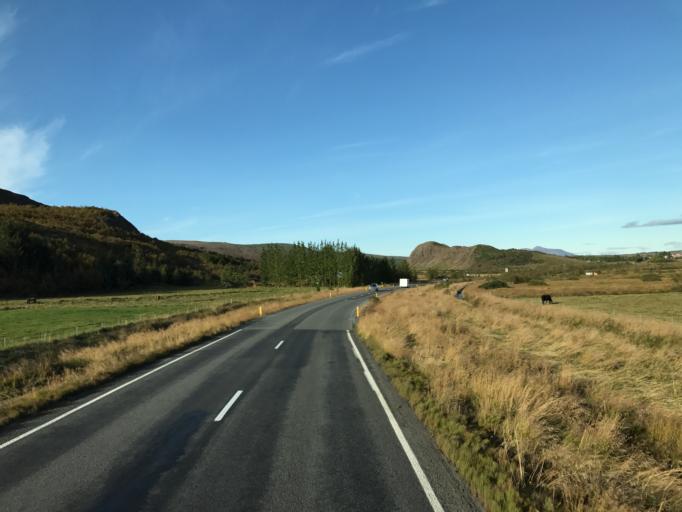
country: IS
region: South
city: Selfoss
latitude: 64.3020
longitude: -20.3298
